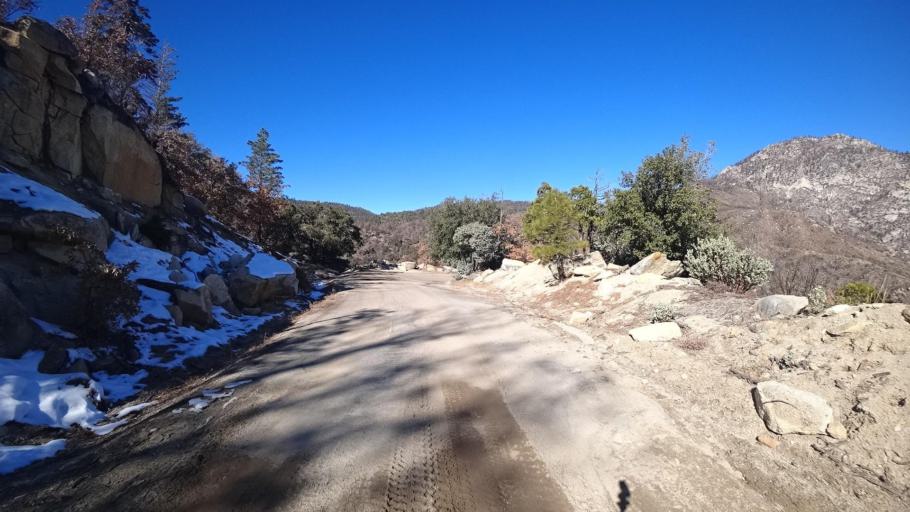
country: US
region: California
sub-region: Kern County
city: Alta Sierra
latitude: 35.7186
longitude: -118.5306
